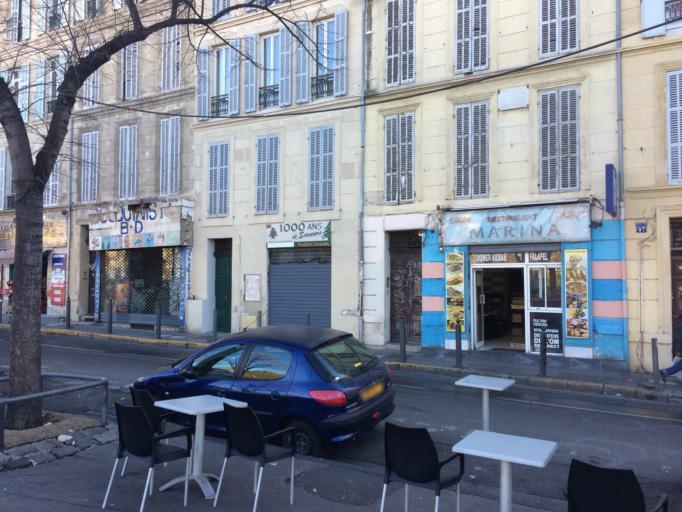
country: FR
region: Provence-Alpes-Cote d'Azur
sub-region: Departement des Bouches-du-Rhone
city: Marseille 01
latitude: 43.2946
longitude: 5.3870
